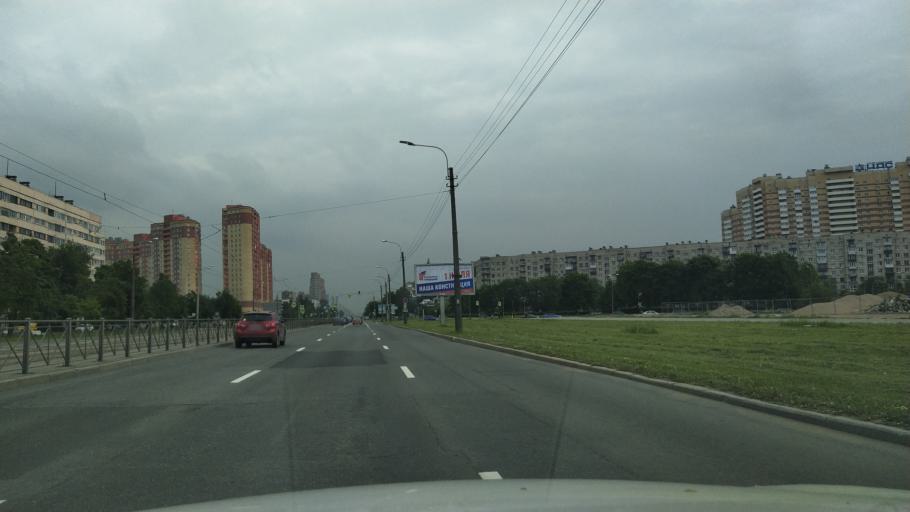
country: RU
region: St.-Petersburg
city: Kupchino
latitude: 59.8696
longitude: 30.3814
